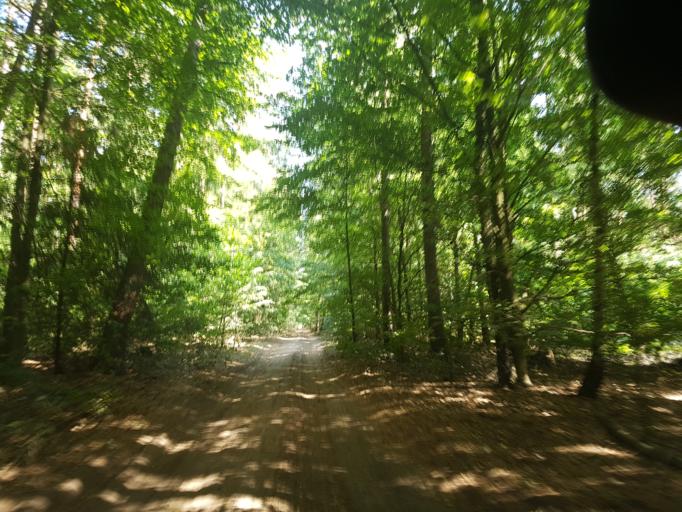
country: DE
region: Brandenburg
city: Gorzke
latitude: 52.0723
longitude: 12.3644
